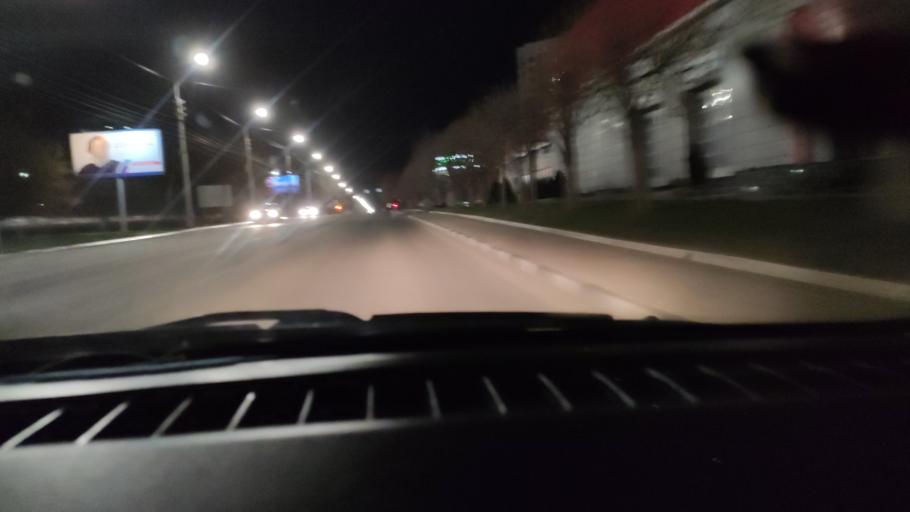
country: RU
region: Saratov
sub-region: Saratovskiy Rayon
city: Saratov
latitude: 51.5710
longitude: 45.9943
